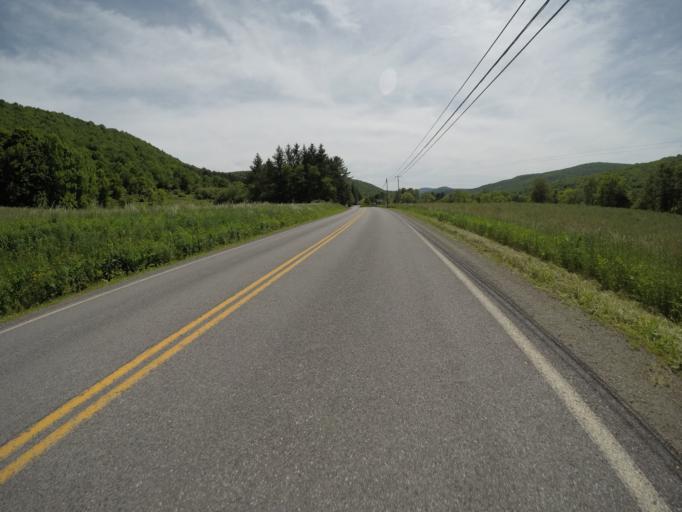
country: US
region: New York
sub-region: Delaware County
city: Delhi
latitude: 42.1320
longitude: -74.8033
